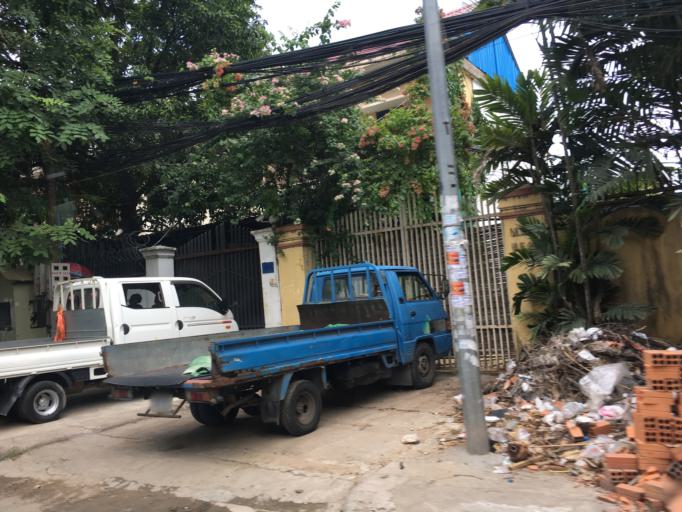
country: KH
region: Phnom Penh
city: Phnom Penh
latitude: 11.5381
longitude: 104.9240
